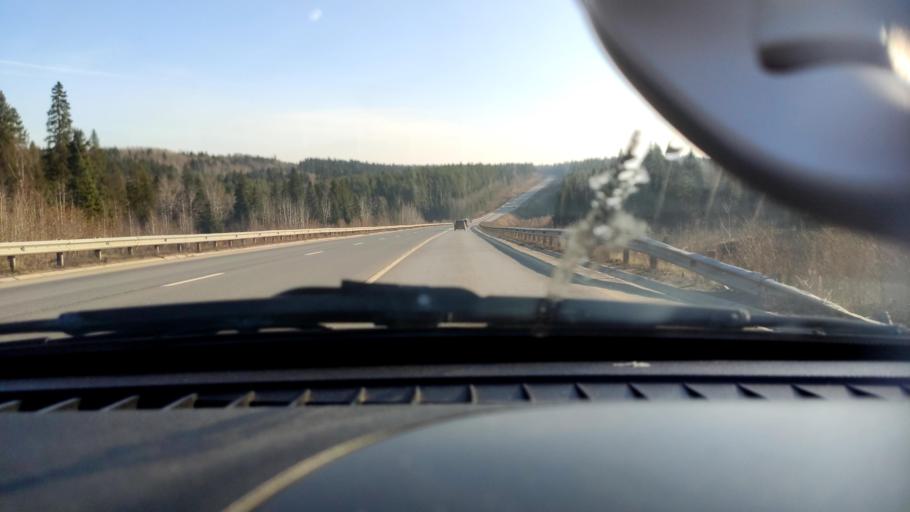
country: RU
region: Perm
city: Novyye Lyady
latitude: 58.0397
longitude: 56.4620
